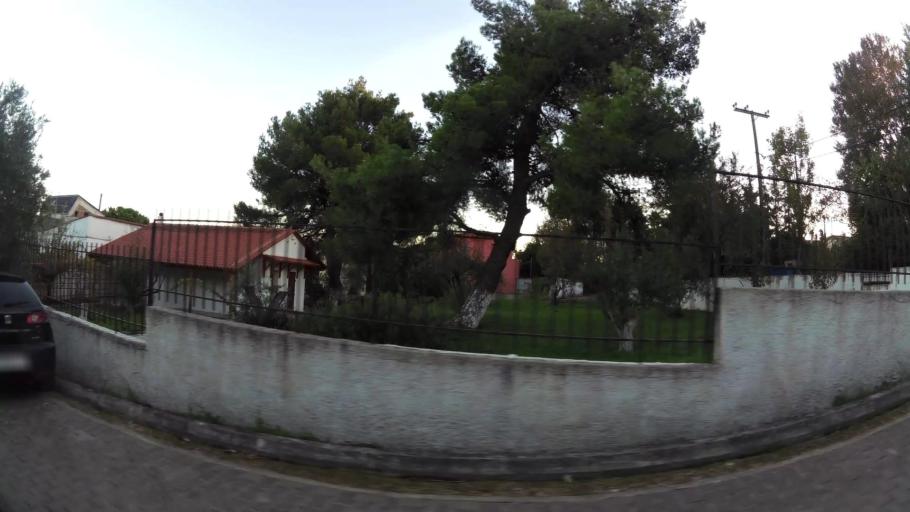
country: GR
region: Attica
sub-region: Nomarchia Anatolikis Attikis
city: Kryoneri
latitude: 38.1451
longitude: 23.8335
